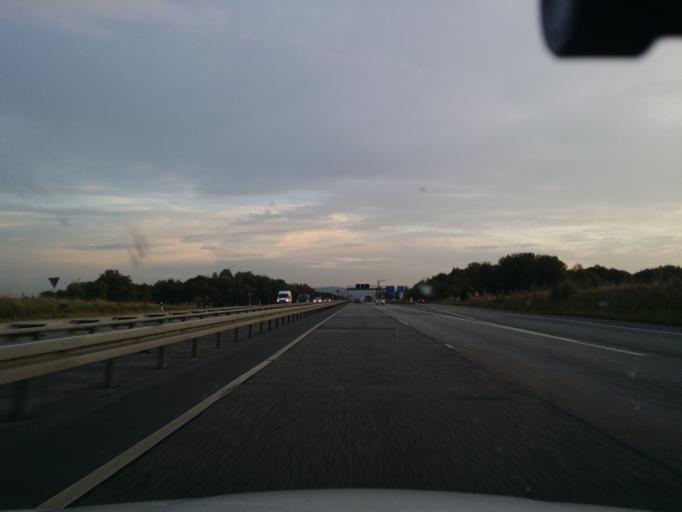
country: DE
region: Hesse
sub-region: Regierungsbezirk Darmstadt
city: Rockenberg
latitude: 50.4777
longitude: 8.7285
